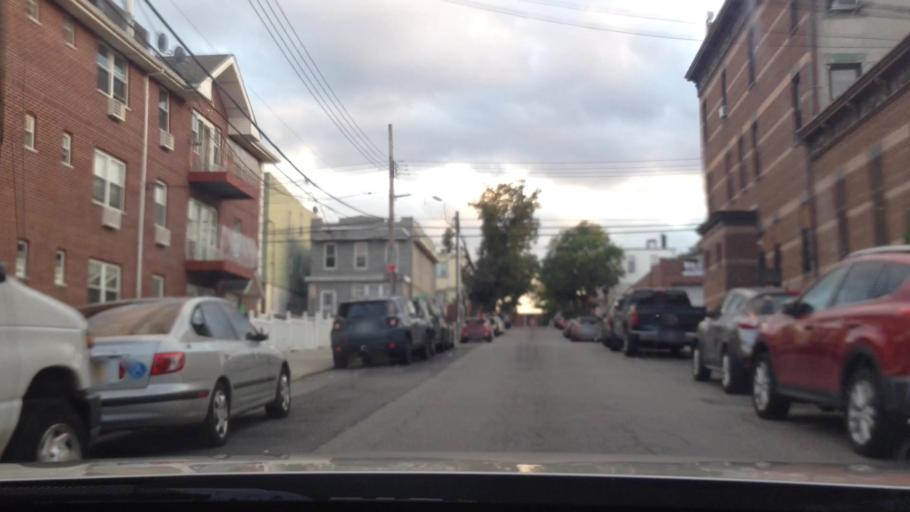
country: US
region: New York
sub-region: Queens County
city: Long Island City
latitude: 40.7250
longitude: -73.9062
